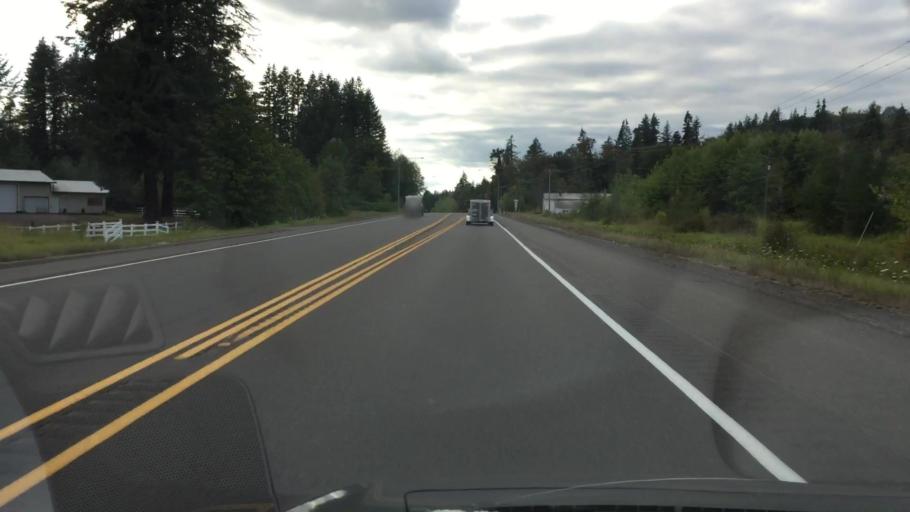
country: US
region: Washington
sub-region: Lewis County
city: Napavine
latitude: 46.5242
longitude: -122.5932
